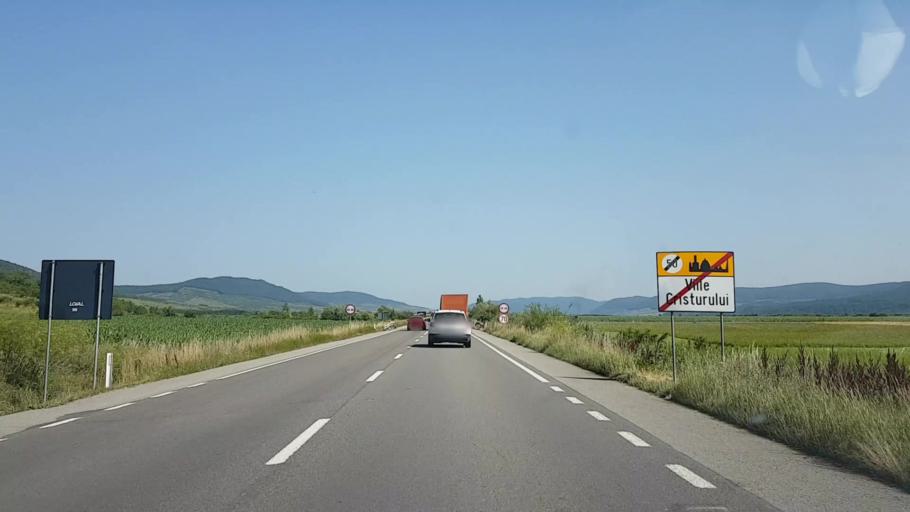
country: RO
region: Bistrita-Nasaud
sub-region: Comuna Sieu-Odorhei
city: Sieu-Odorhei
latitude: 47.1274
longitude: 24.3171
